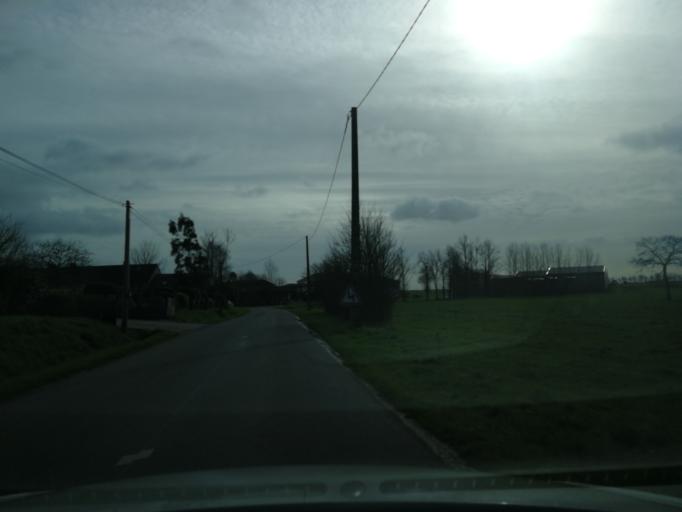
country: FR
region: Brittany
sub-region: Departement d'Ille-et-Vilaine
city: Bourg-des-Comptes
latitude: 47.9147
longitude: -1.7096
